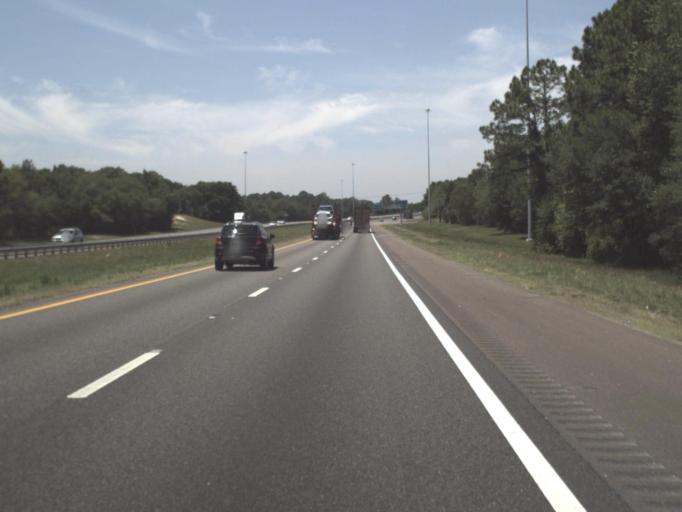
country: US
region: Florida
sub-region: Duval County
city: Jacksonville
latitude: 30.4452
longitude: -81.6044
